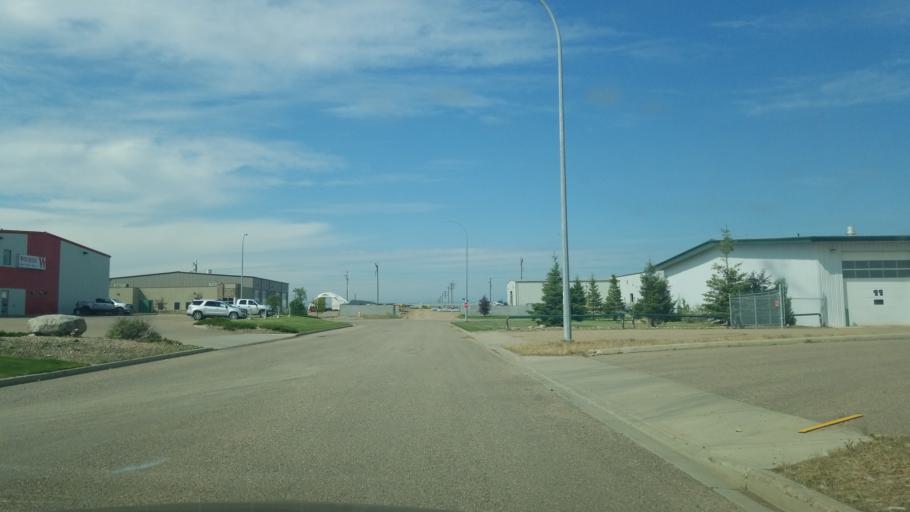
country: CA
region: Saskatchewan
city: Lloydminster
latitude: 53.2905
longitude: -110.0419
